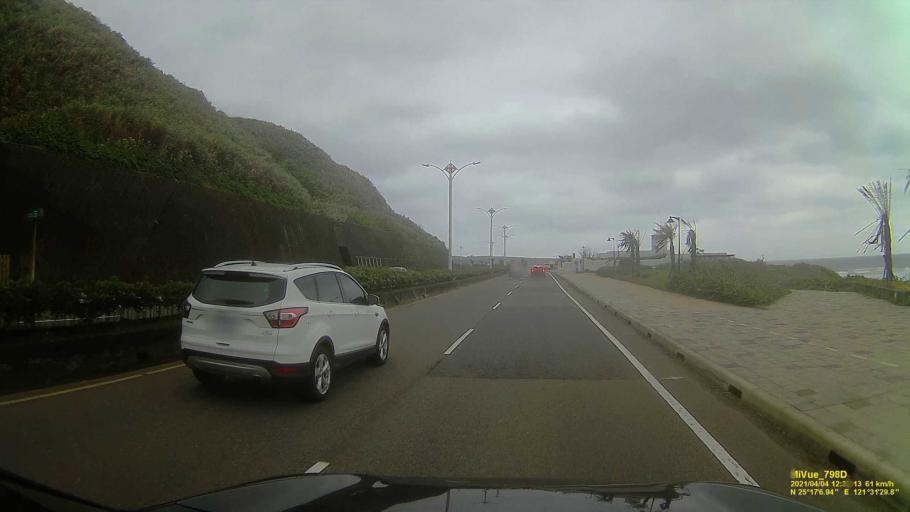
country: TW
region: Taipei
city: Taipei
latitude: 25.2853
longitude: 121.5247
